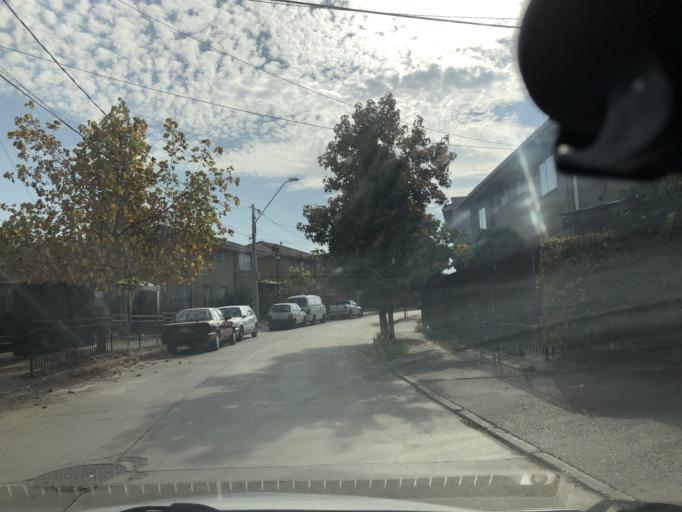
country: CL
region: Santiago Metropolitan
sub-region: Provincia de Cordillera
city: Puente Alto
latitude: -33.5957
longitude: -70.5429
